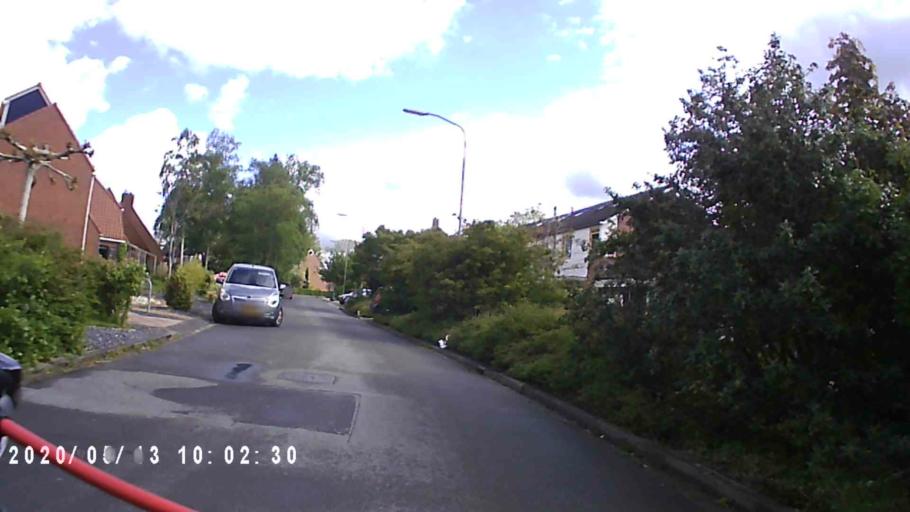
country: NL
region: Groningen
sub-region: Gemeente Zuidhorn
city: Zuidhorn
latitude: 53.2430
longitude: 6.3967
